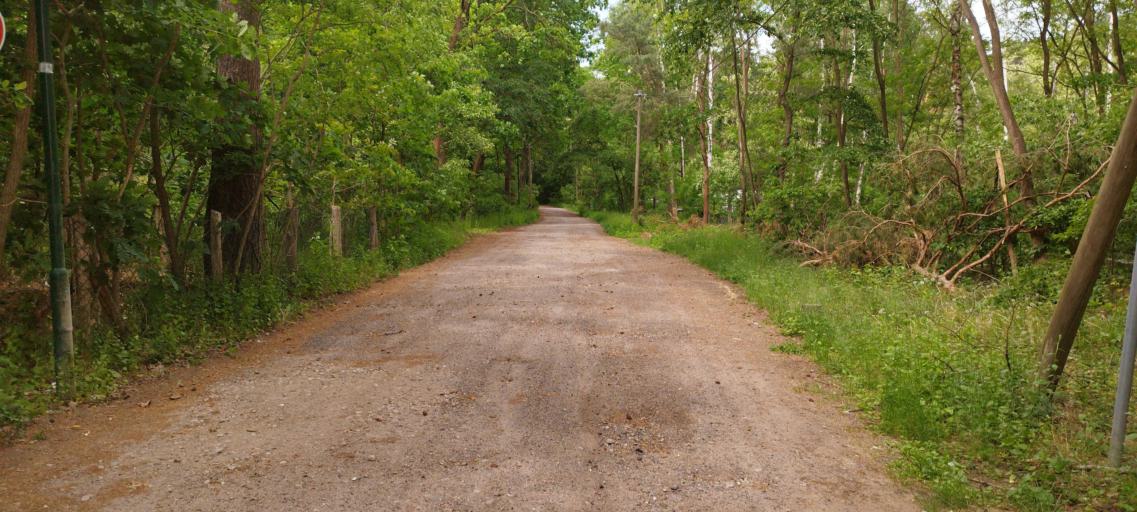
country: DE
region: Brandenburg
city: Furstenwalde
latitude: 52.3357
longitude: 14.0557
